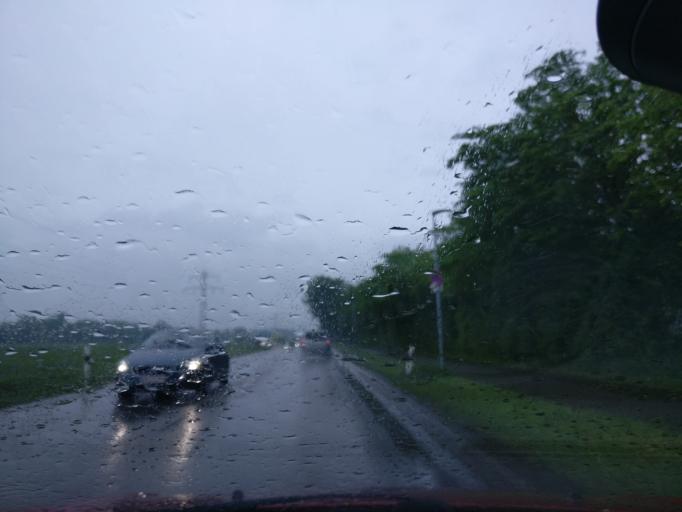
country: DE
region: Bavaria
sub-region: Upper Bavaria
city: Dachau
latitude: 48.2540
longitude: 11.4555
